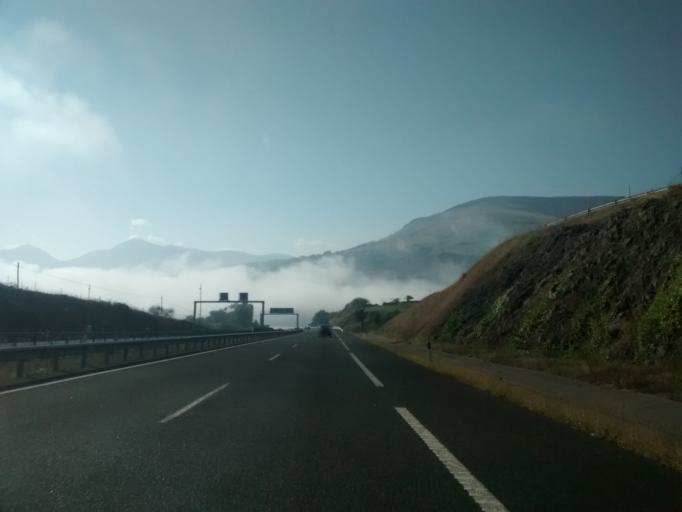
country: ES
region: Cantabria
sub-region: Provincia de Cantabria
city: Arenas de Iguna
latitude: 43.2000
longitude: -4.0722
